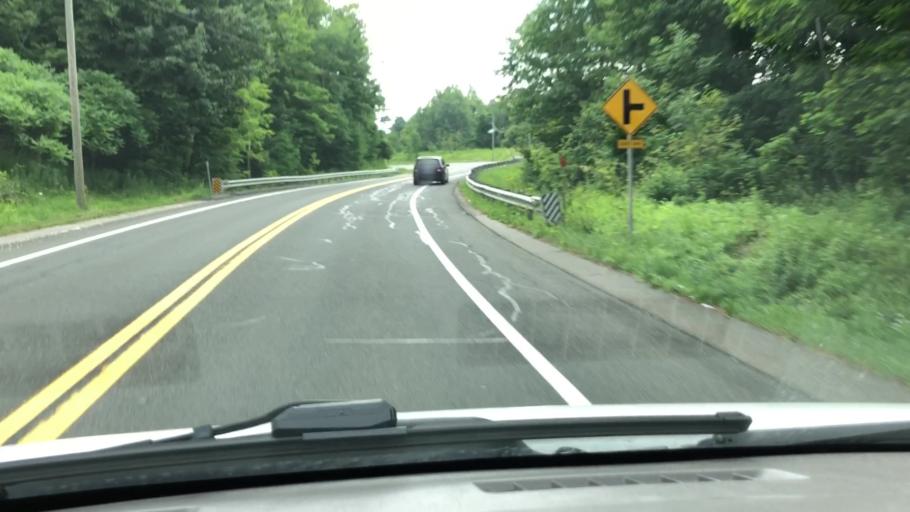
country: US
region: Massachusetts
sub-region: Berkshire County
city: Lanesborough
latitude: 42.4964
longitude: -73.2329
